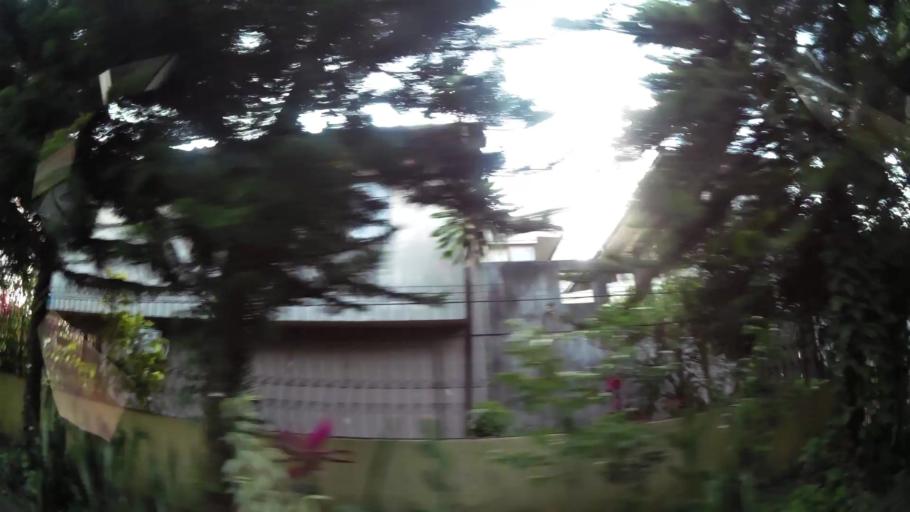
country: CO
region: Valle del Cauca
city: Cali
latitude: 3.4052
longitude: -76.5538
